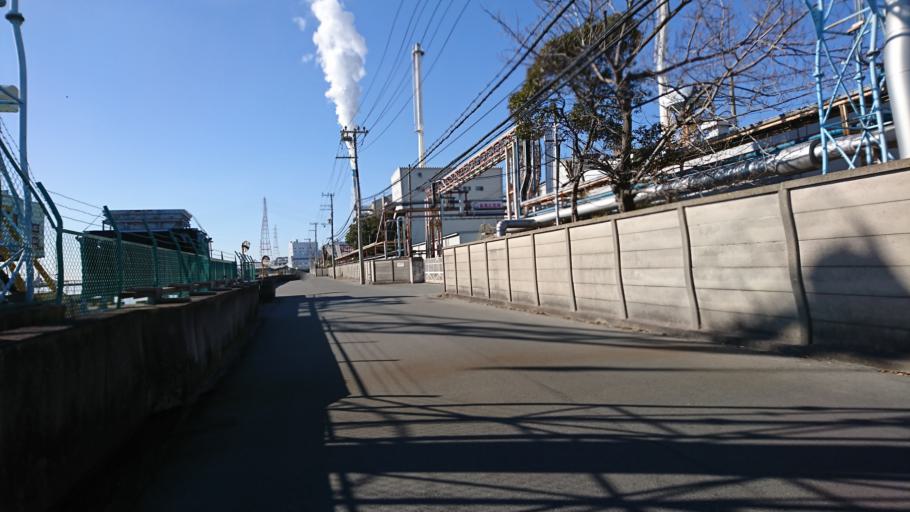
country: JP
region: Hyogo
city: Kakogawacho-honmachi
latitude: 34.7603
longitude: 134.7729
